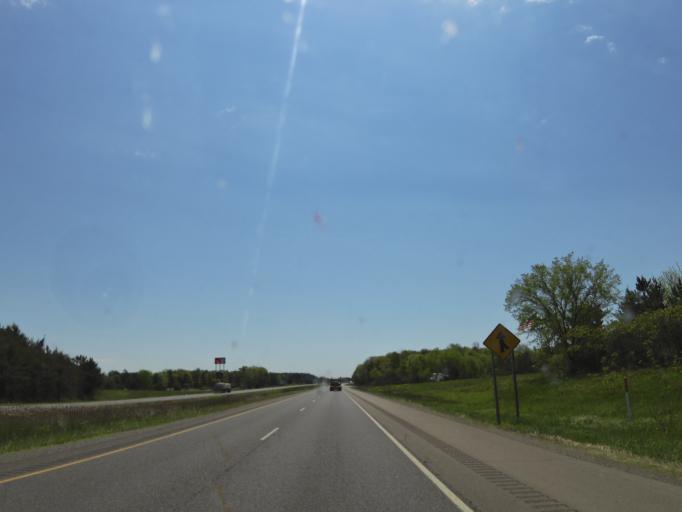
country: US
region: Wisconsin
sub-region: Jackson County
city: Black River Falls
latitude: 44.2958
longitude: -90.8229
